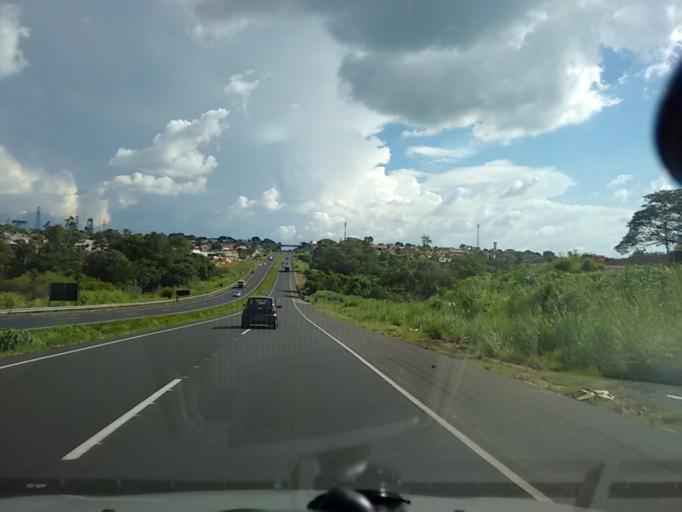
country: BR
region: Sao Paulo
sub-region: Marilia
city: Marilia
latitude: -22.2152
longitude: -49.9645
